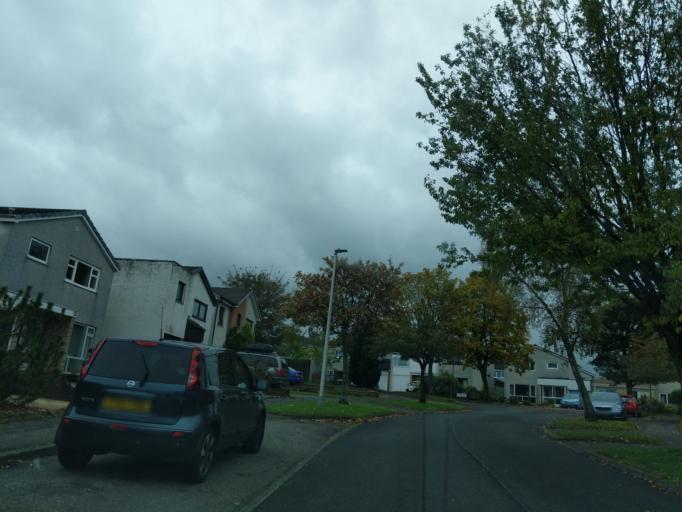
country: GB
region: Scotland
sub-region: Edinburgh
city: Balerno
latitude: 55.8782
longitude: -3.3475
